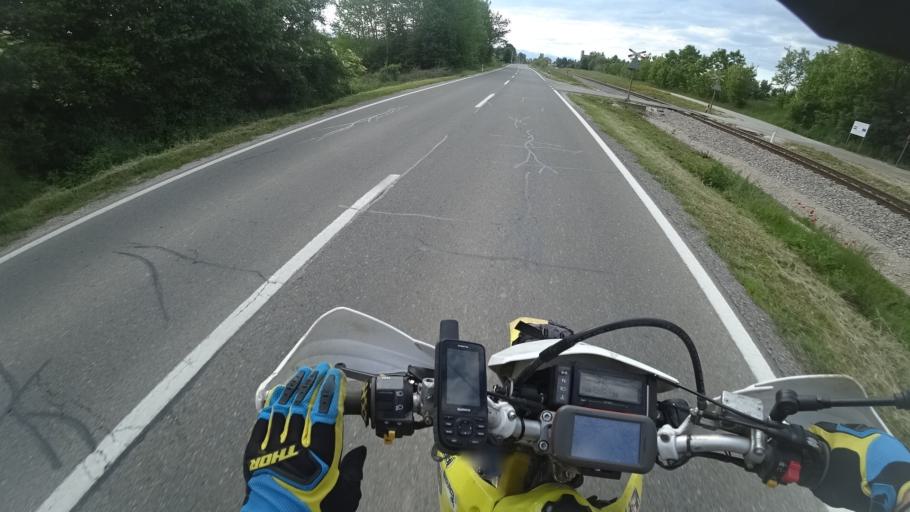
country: HR
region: Licko-Senjska
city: Gospic
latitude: 44.5277
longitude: 15.4076
